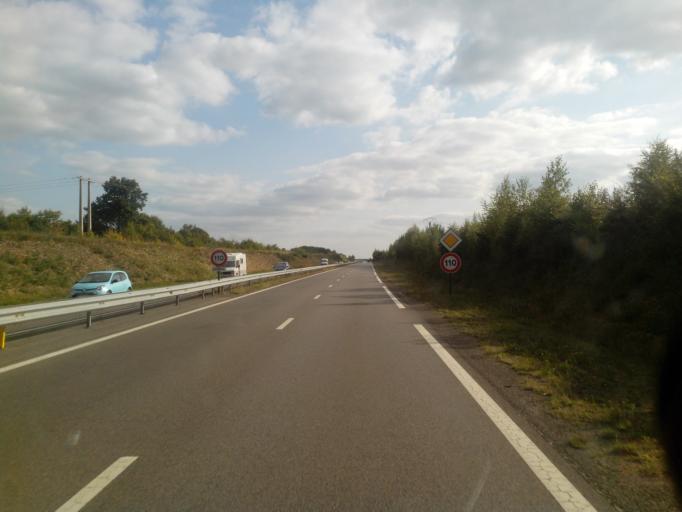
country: FR
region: Brittany
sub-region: Departement d'Ille-et-Vilaine
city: Betton
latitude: 48.1772
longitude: -1.6254
